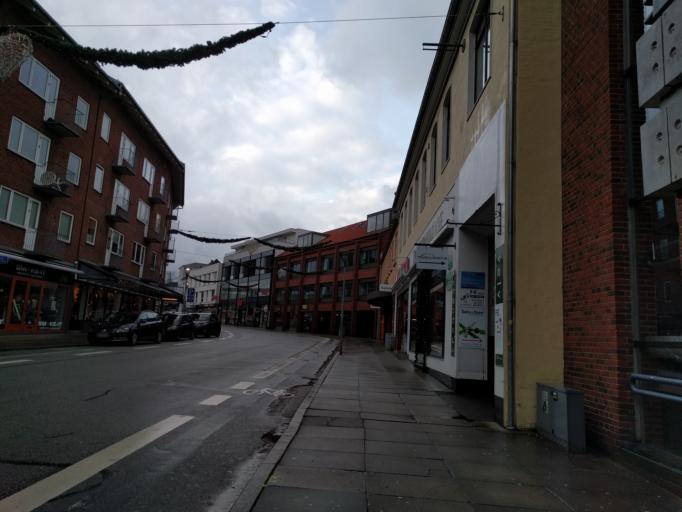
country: DK
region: Central Jutland
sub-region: Silkeborg Kommune
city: Silkeborg
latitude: 56.1705
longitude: 9.5513
